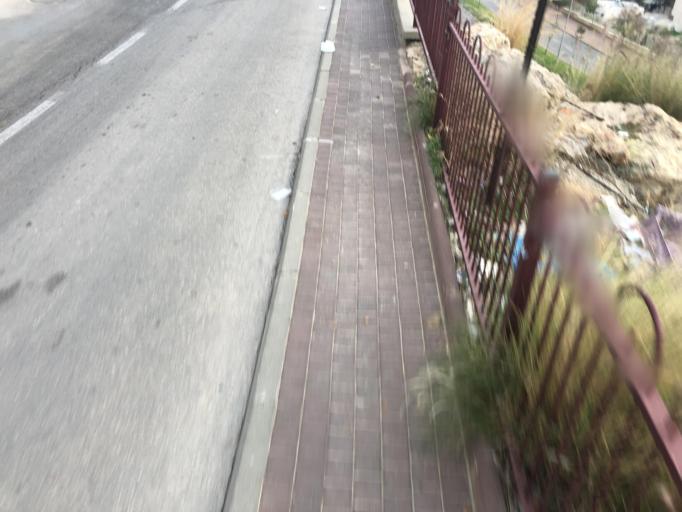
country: IL
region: Jerusalem
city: Modiin Ilit
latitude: 31.9368
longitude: 35.0432
